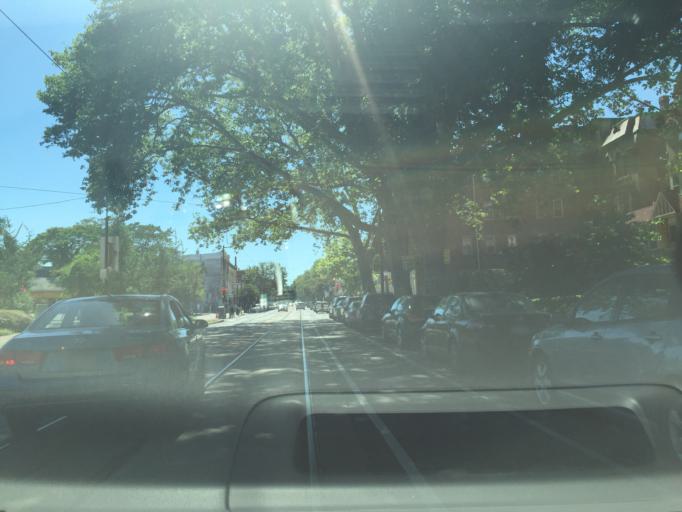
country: US
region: Pennsylvania
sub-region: Delaware County
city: Millbourne
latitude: 39.9492
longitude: -75.2120
